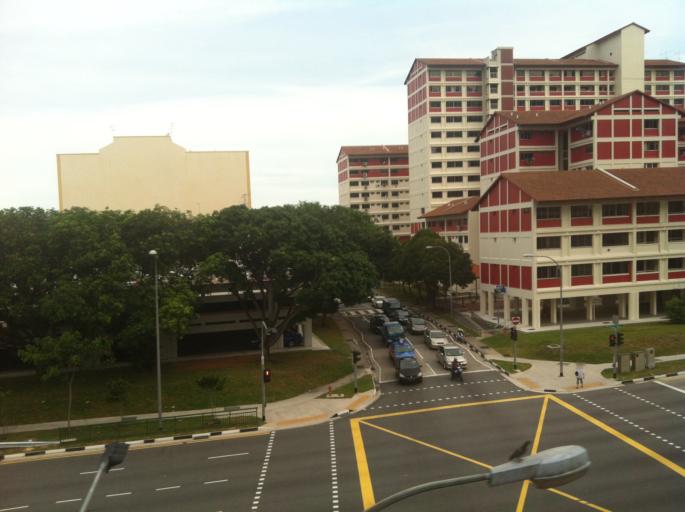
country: SG
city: Singapore
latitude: 1.3131
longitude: 103.8743
